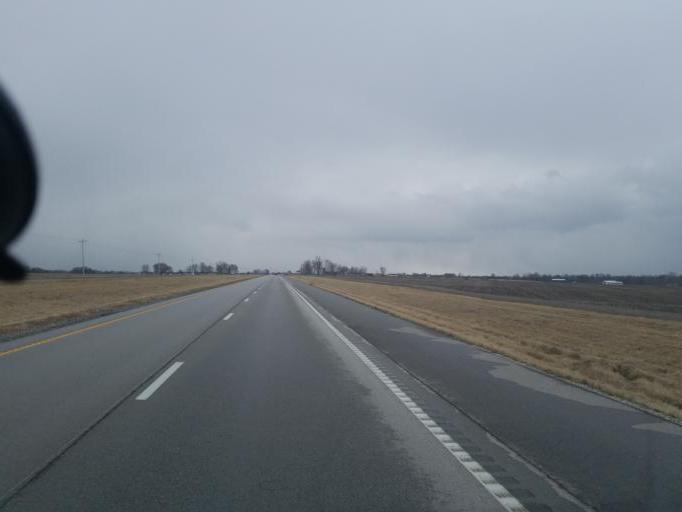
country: US
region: Missouri
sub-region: Macon County
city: Macon
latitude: 39.8303
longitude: -92.4747
